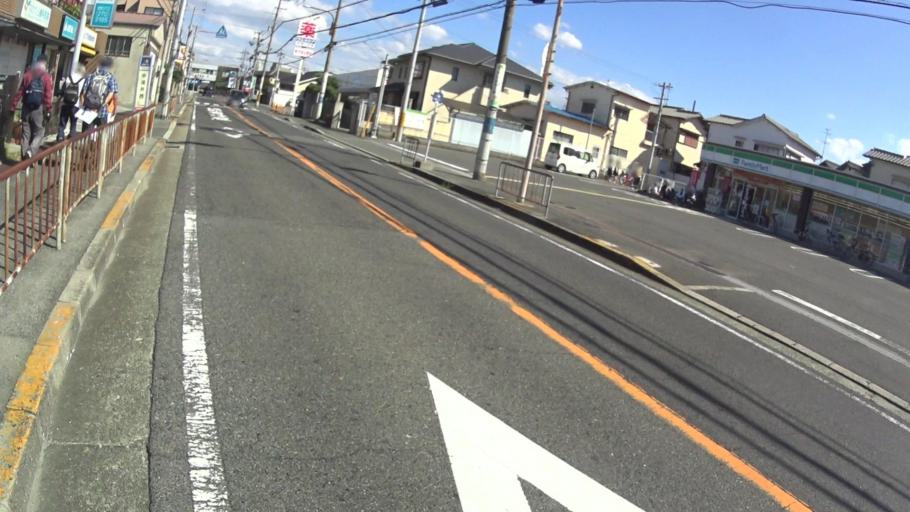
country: JP
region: Ehime
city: Kihoku-cho
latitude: 33.3720
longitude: 132.8010
